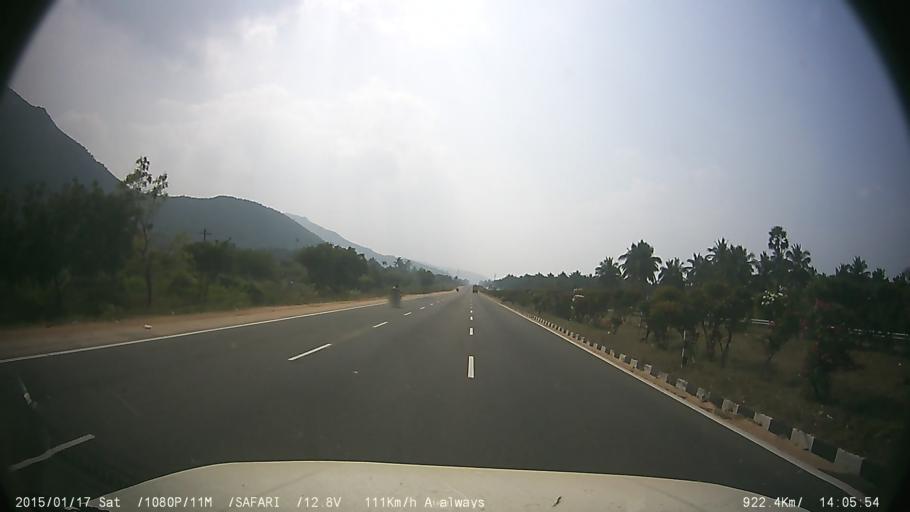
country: IN
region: Tamil Nadu
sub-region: Vellore
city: Ambur
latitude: 12.8443
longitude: 78.8008
